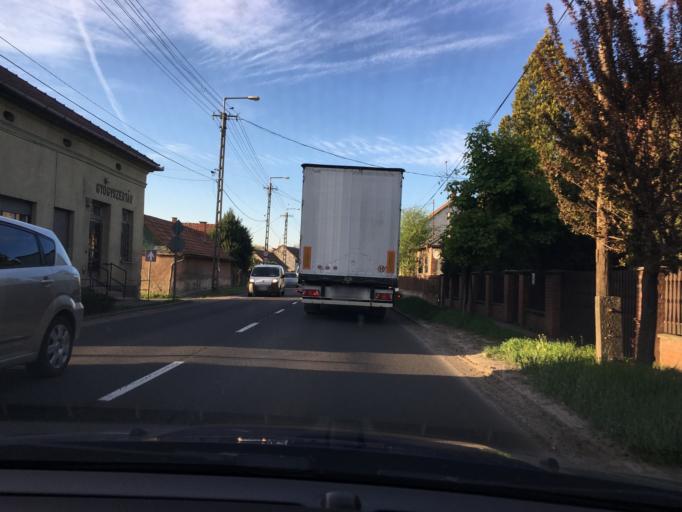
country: HU
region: Hajdu-Bihar
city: Mikepercs
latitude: 47.4407
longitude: 21.6316
